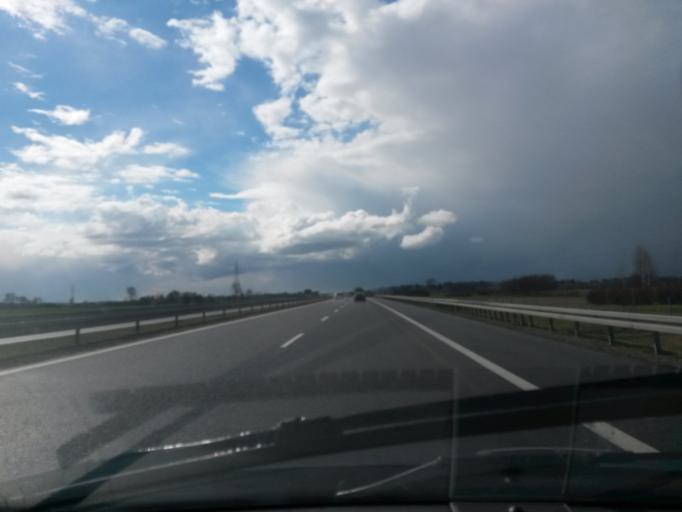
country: PL
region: Greater Poland Voivodeship
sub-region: Powiat wrzesinski
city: Wrzesnia
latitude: 52.3179
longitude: 17.5115
